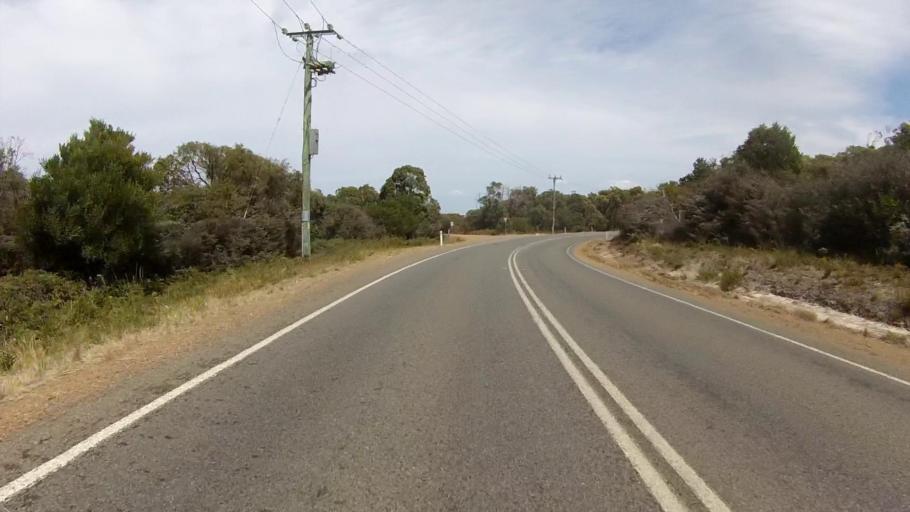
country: AU
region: Tasmania
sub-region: Clarence
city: Sandford
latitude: -43.0230
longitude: 147.4873
